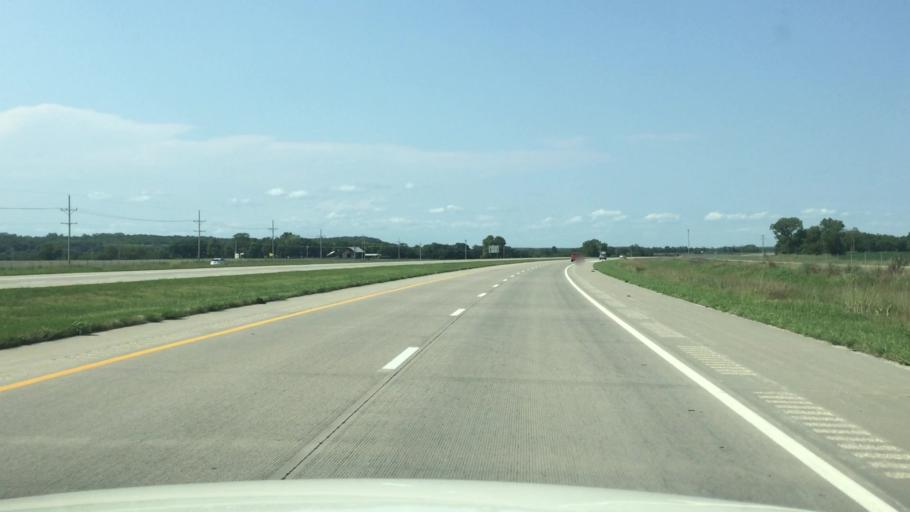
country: US
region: Kansas
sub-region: Linn County
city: Pleasanton
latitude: 38.1915
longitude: -94.7047
